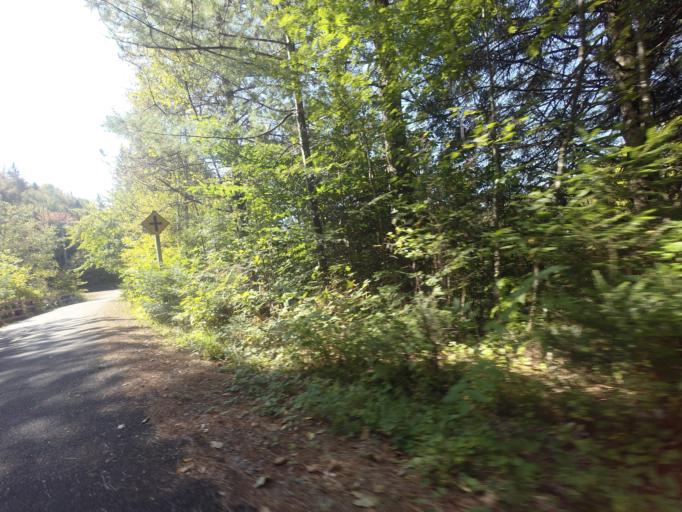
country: CA
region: Quebec
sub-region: Laurentides
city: Mont-Tremblant
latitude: 46.1134
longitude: -74.5017
